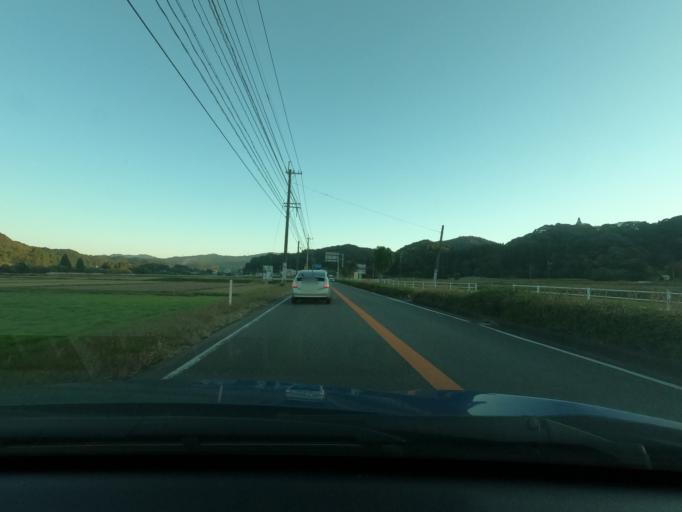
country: JP
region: Kagoshima
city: Satsumasendai
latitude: 31.8022
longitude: 130.3986
